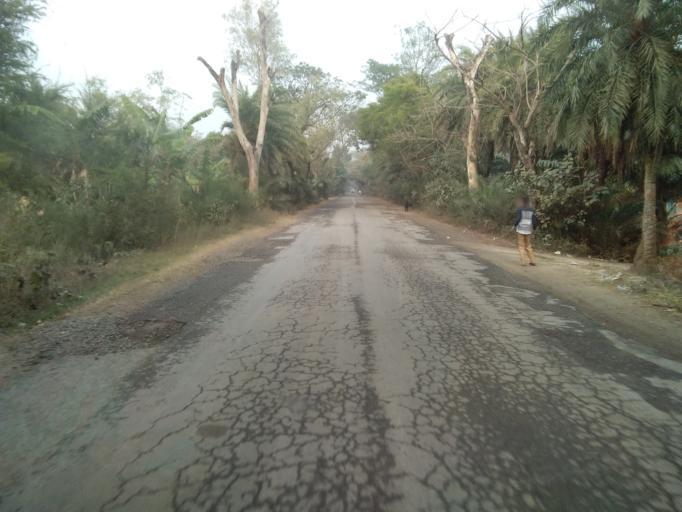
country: BD
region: Khulna
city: Satkhira
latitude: 22.6830
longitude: 89.0270
